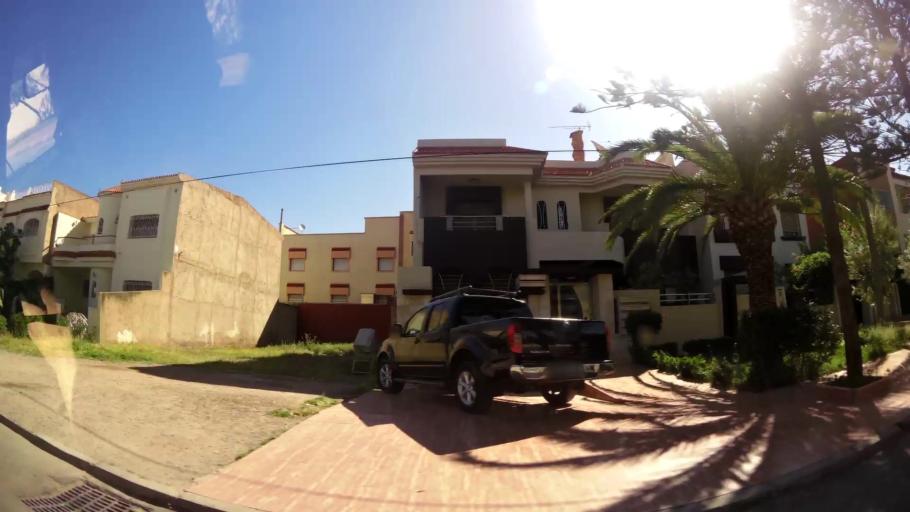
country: MA
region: Oriental
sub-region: Oujda-Angad
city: Oujda
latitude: 34.6597
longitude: -1.8945
